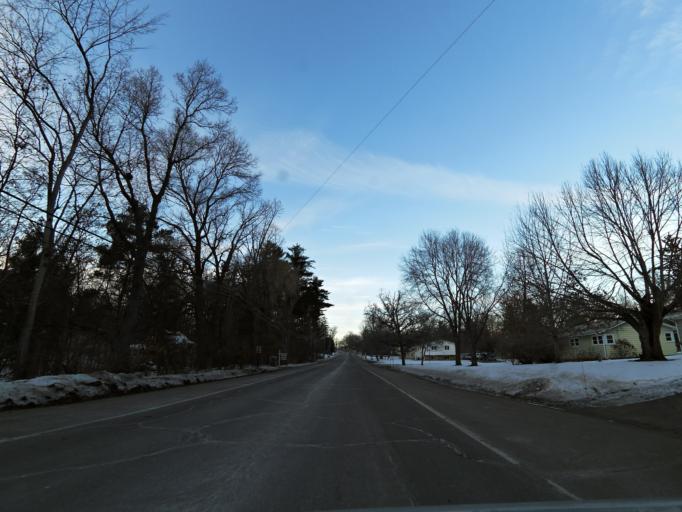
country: US
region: Minnesota
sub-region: Washington County
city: Lake Elmo
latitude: 44.9941
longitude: -92.8794
